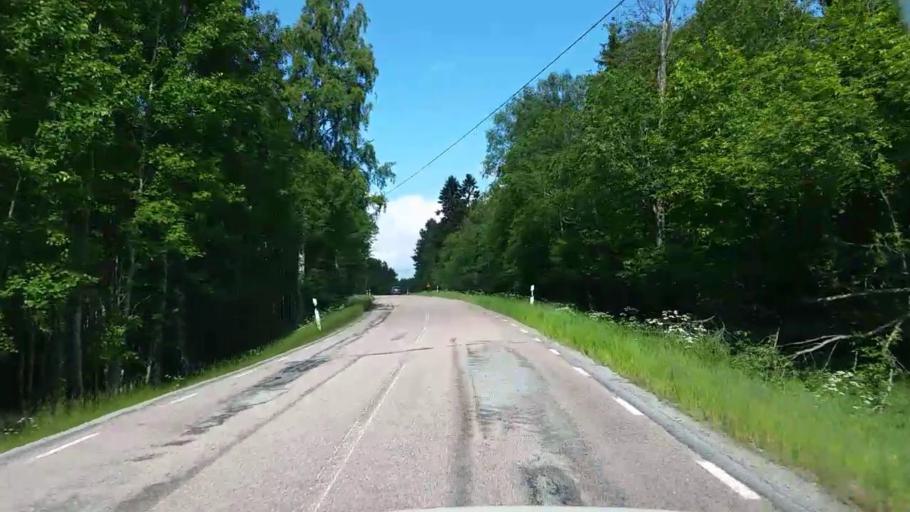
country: SE
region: Vaestmanland
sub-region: Fagersta Kommun
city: Fagersta
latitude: 59.9450
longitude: 15.8006
